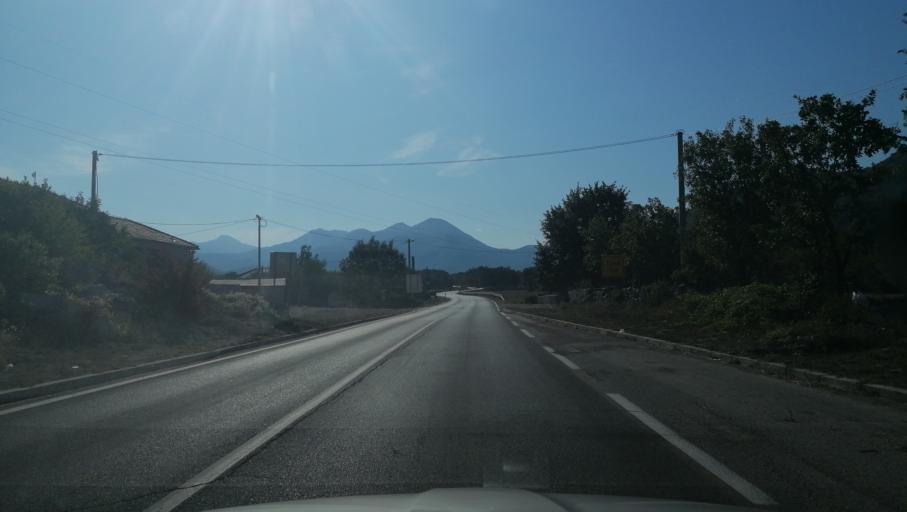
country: BA
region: Republika Srpska
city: Trebinje
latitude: 42.6483
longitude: 18.3740
